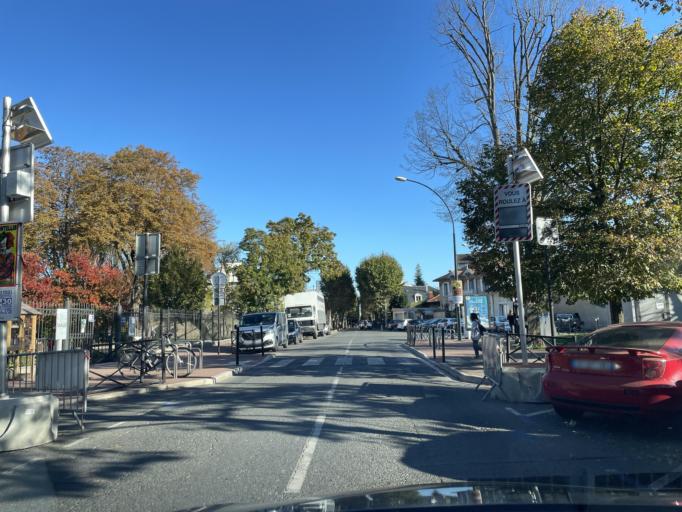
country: FR
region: Ile-de-France
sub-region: Departement du Val-de-Marne
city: Joinville-le-Pont
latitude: 48.8122
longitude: 2.4743
